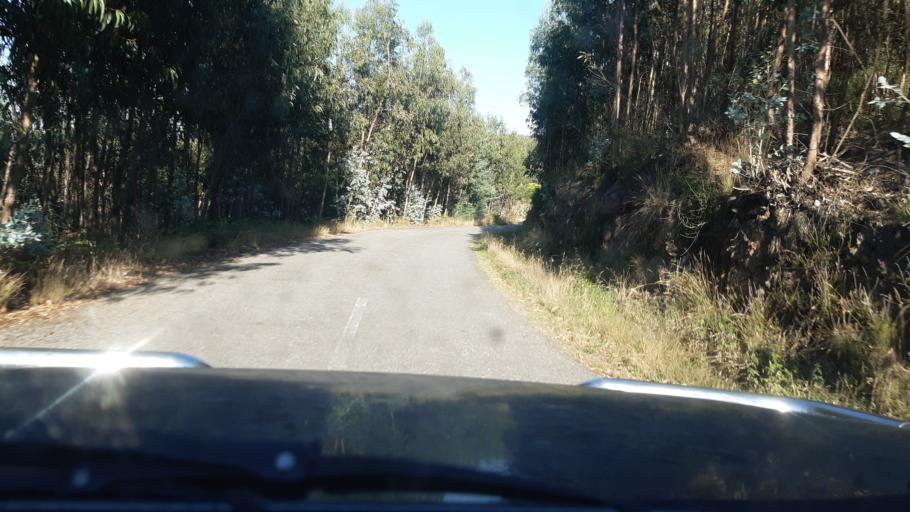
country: PT
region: Aveiro
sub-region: Agueda
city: Aguada de Cima
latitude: 40.5671
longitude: -8.3299
